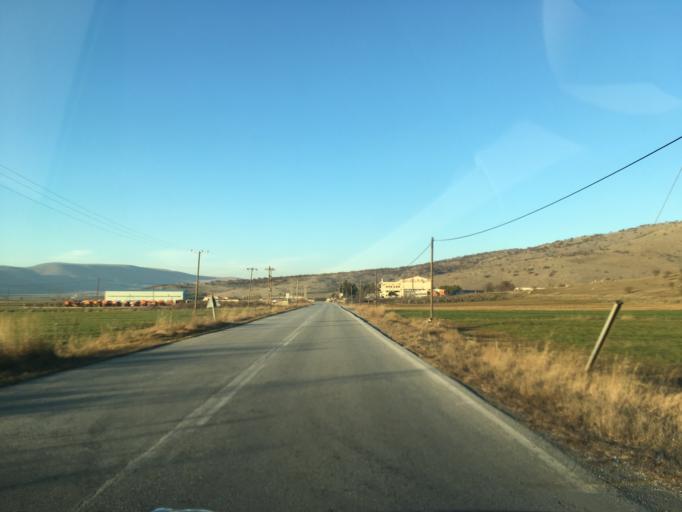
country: GR
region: West Macedonia
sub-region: Nomos Kozanis
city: Kozani
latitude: 40.2941
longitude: 21.7336
